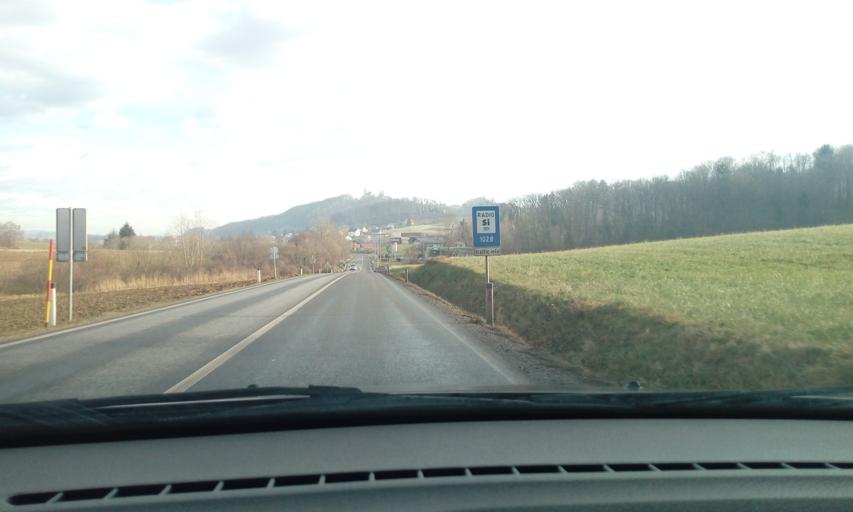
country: SI
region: Smarje pri Jelsah
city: Smarje pri Jelsah
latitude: 46.2296
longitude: 15.5007
